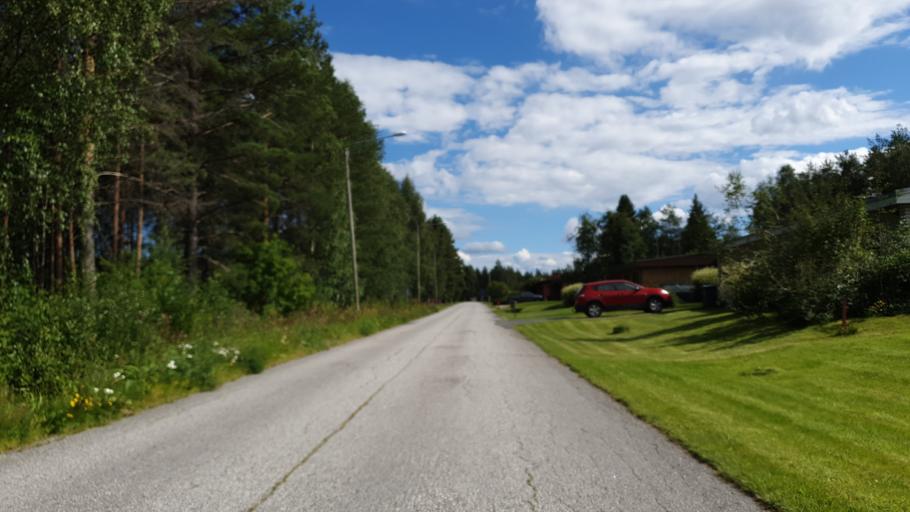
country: FI
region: Kainuu
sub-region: Kehys-Kainuu
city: Kuhmo
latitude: 64.1154
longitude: 29.4871
